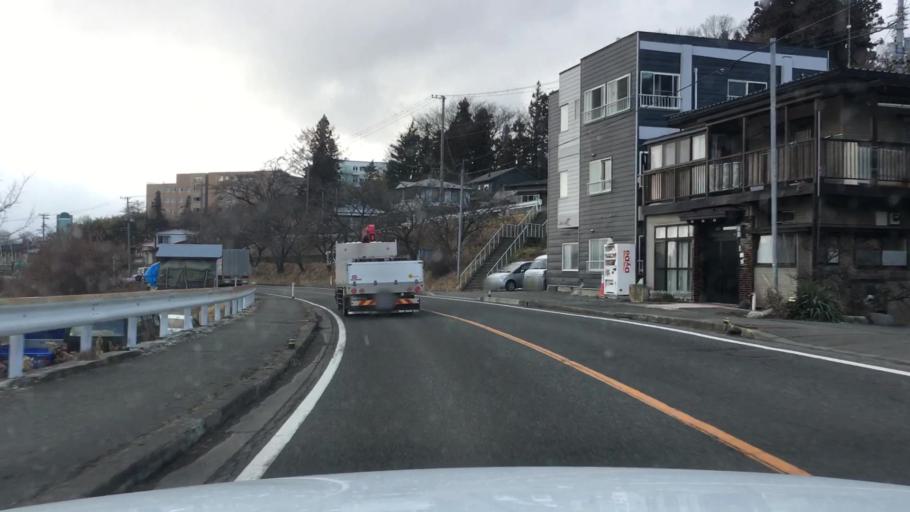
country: JP
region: Iwate
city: Morioka-shi
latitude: 39.6864
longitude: 141.1816
